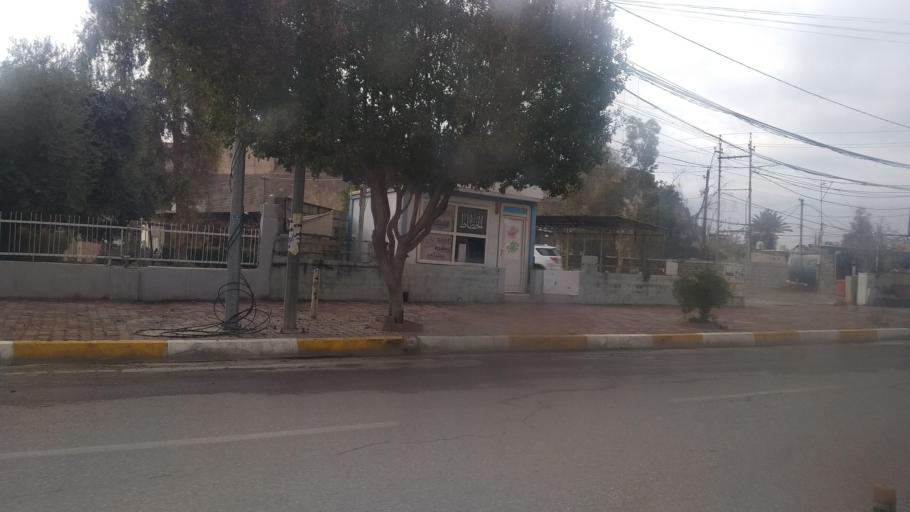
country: IQ
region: Arbil
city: Erbil
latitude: 36.1945
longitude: 44.0117
